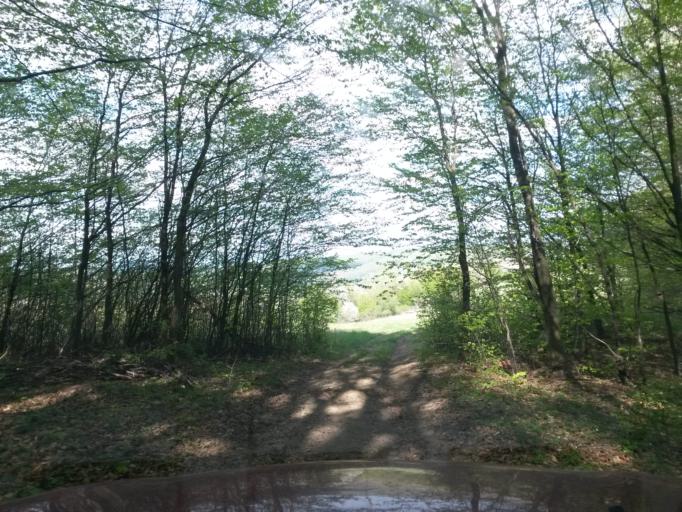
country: SK
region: Presovsky
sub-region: Okres Presov
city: Presov
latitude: 48.9498
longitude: 21.1425
